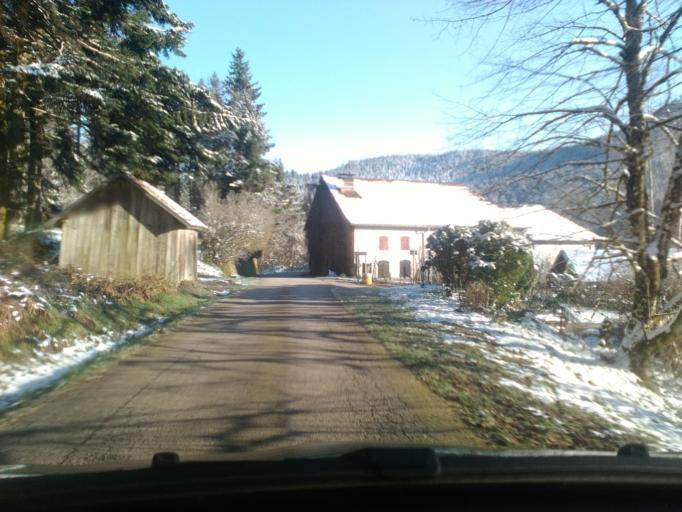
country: FR
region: Lorraine
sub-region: Departement des Vosges
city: Taintrux
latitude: 48.2323
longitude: 6.8614
